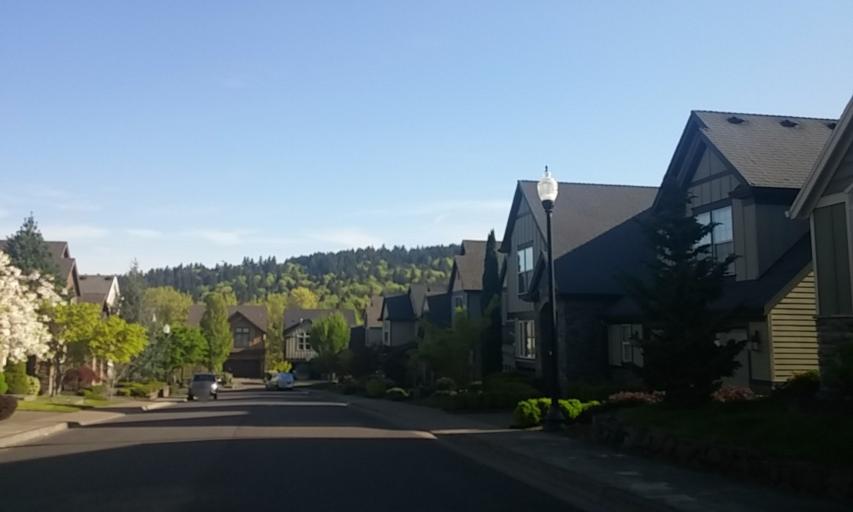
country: US
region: Oregon
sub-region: Washington County
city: Cedar Mill
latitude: 45.5470
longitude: -122.7912
